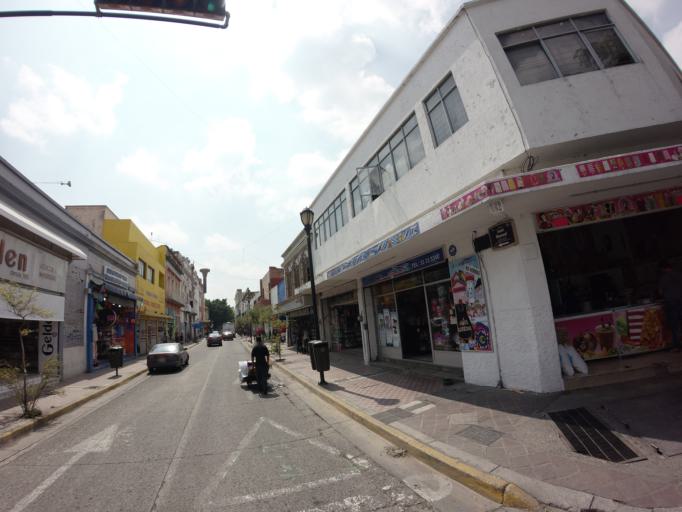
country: MX
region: Jalisco
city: Guadalajara
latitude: 20.6787
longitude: -103.3513
